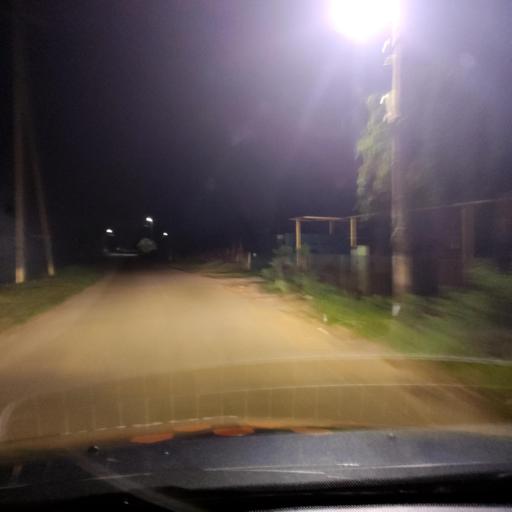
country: RU
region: Voronezj
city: Novaya Usman'
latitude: 51.6378
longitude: 39.3885
